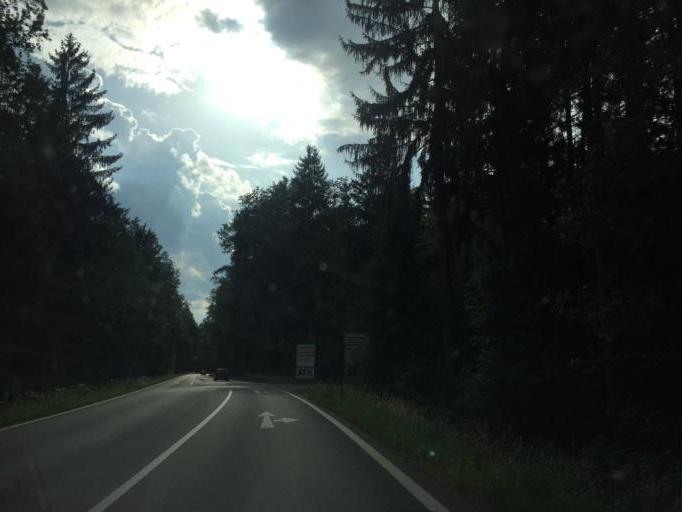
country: AT
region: Styria
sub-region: Politischer Bezirk Leibnitz
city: Sankt Veit am Vogau
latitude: 46.7576
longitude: 15.6330
